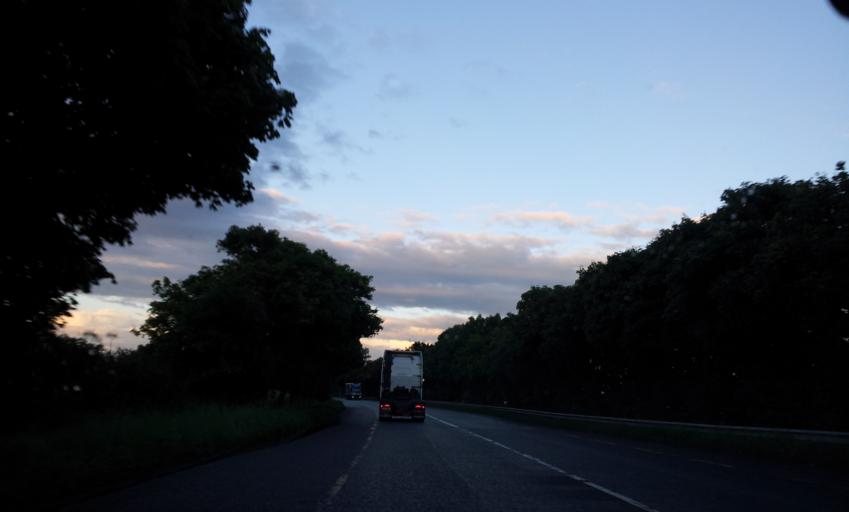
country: IE
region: Munster
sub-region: County Limerick
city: Rathkeale
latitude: 52.5284
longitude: -8.8938
